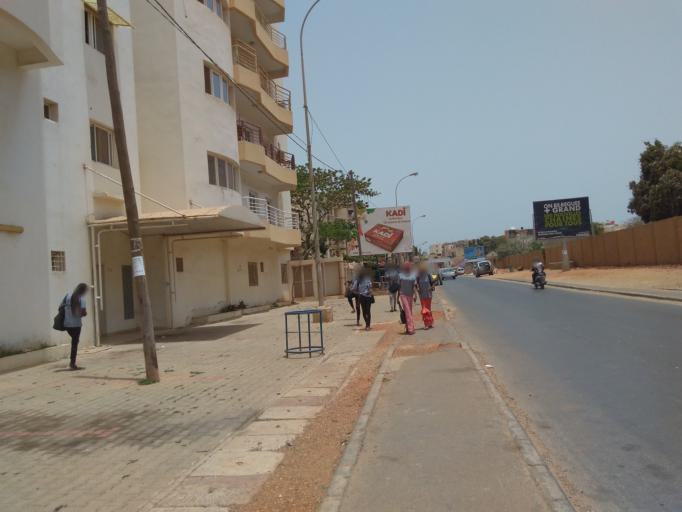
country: SN
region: Dakar
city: Grand Dakar
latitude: 14.7316
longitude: -17.4695
